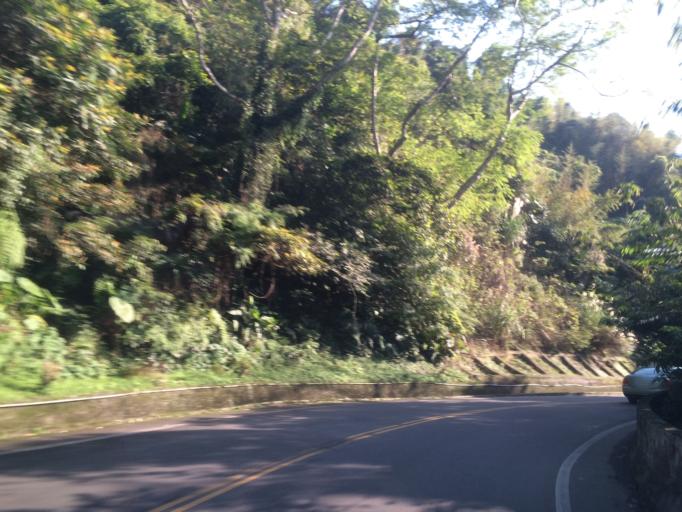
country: TW
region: Taiwan
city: Daxi
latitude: 24.8123
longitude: 121.2580
